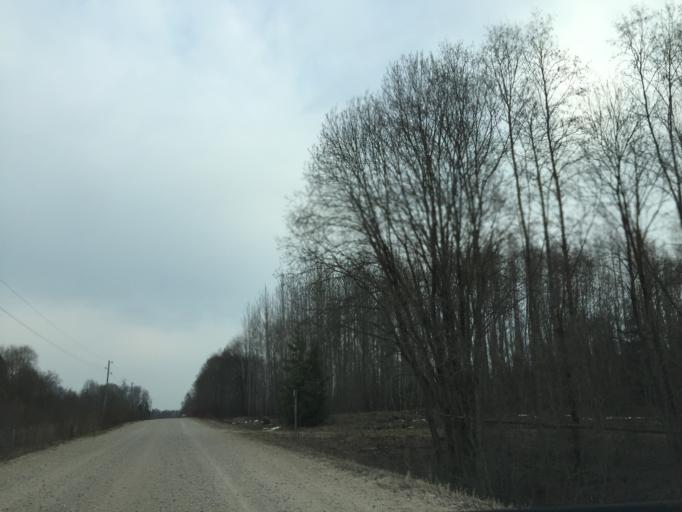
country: LV
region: Priekuli
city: Priekuli
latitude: 57.1812
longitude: 25.4733
